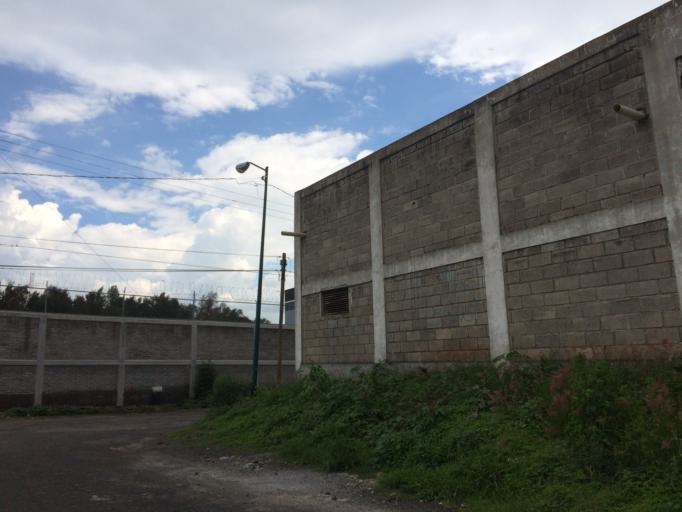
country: MX
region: Michoacan
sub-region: Morelia
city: Morelos
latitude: 19.6834
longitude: -101.2335
